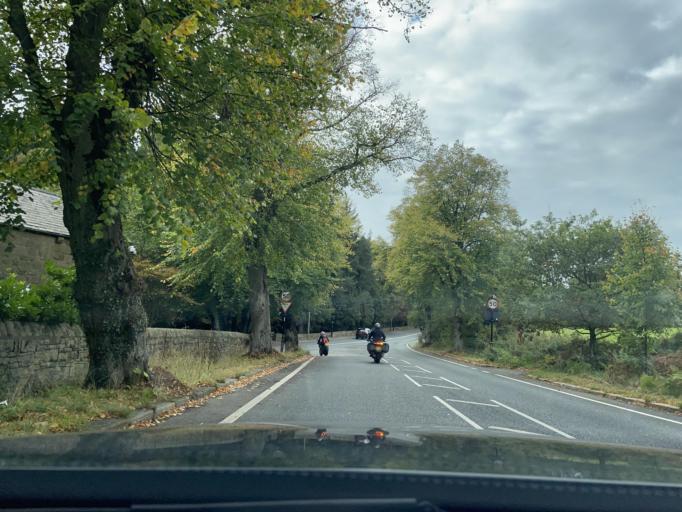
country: GB
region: England
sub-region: Sheffield
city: Bradfield
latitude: 53.3804
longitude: -1.5668
